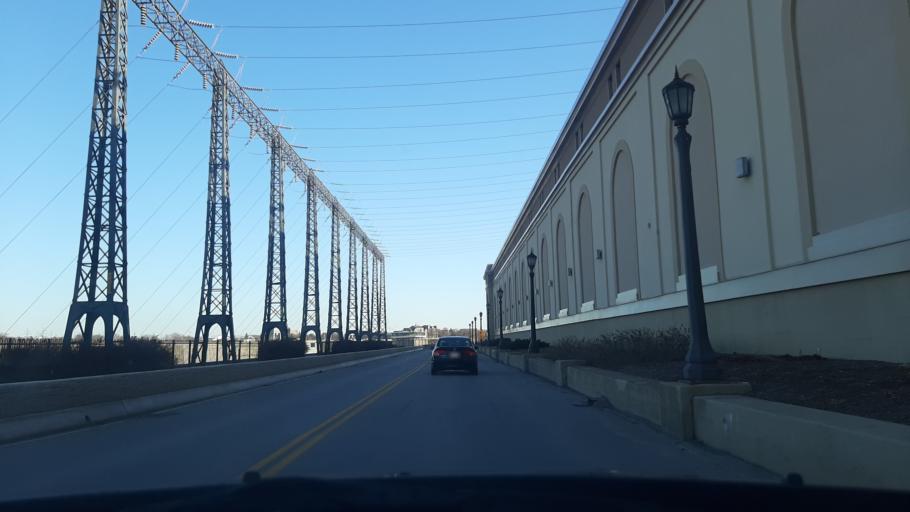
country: US
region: New York
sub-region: Niagara County
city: Lewiston
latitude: 43.1498
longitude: -79.0461
